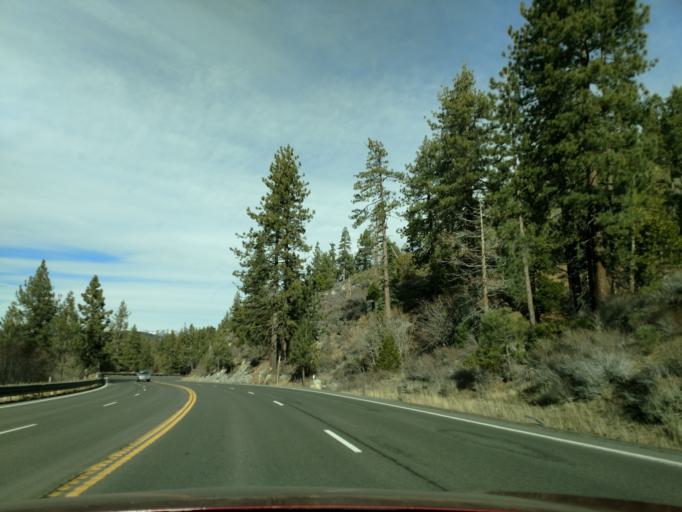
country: US
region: Nevada
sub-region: Douglas County
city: Kingsbury
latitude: 39.0589
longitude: -119.9425
